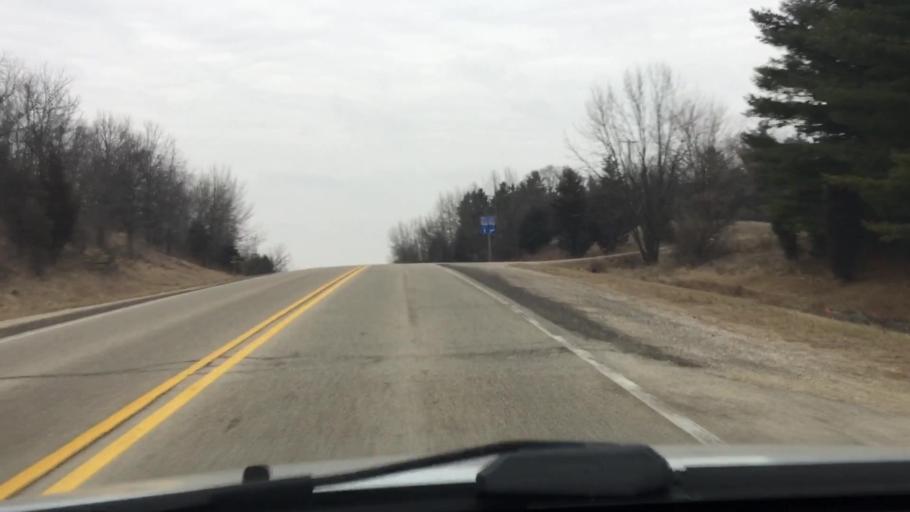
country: US
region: Wisconsin
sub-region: Waukesha County
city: Delafield
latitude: 43.0498
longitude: -88.4044
